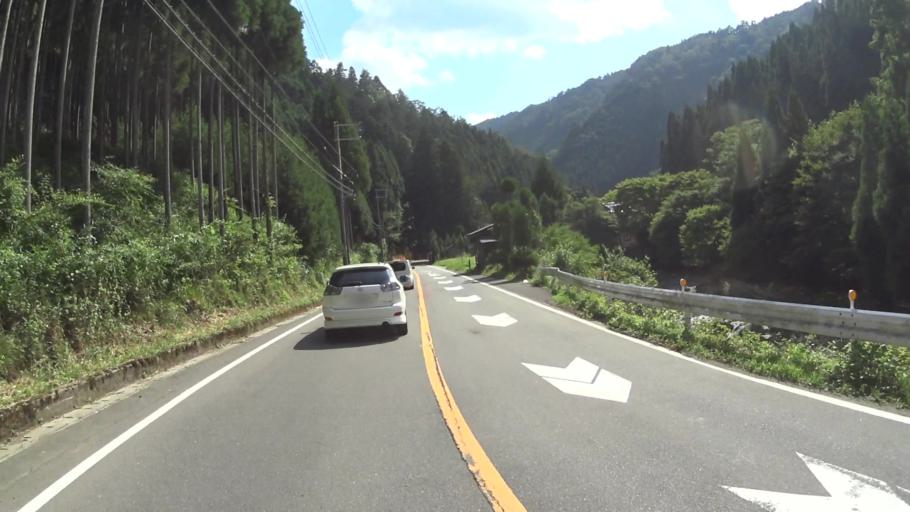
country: JP
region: Kyoto
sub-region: Kyoto-shi
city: Kamigyo-ku
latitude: 35.1068
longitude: 135.6800
